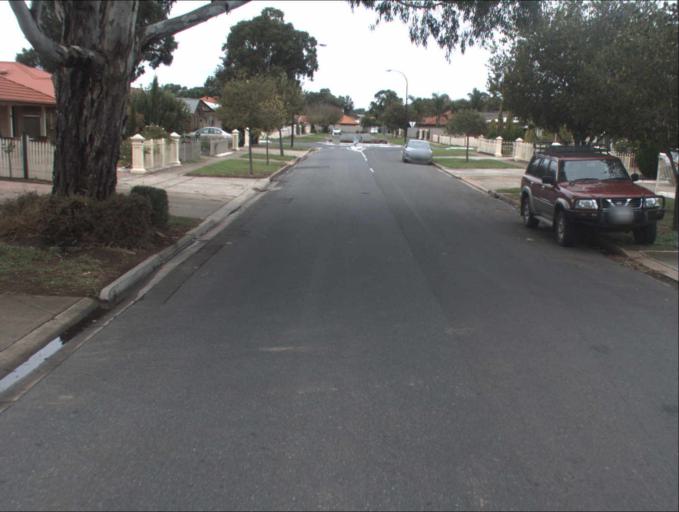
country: AU
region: South Australia
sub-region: Charles Sturt
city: Woodville North
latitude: -34.8681
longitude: 138.5610
